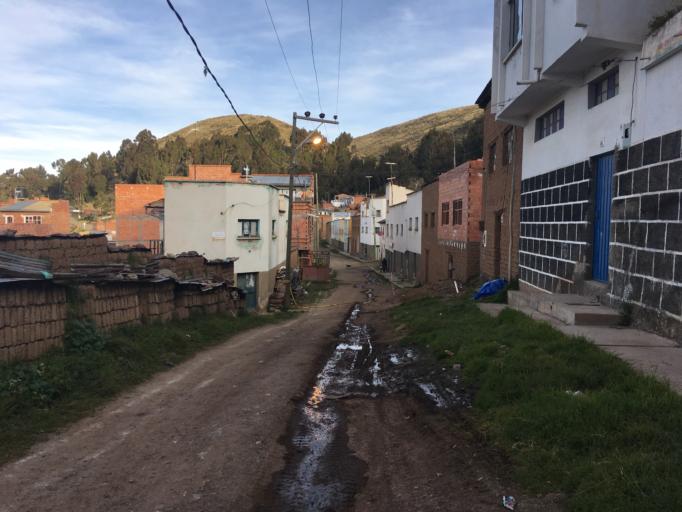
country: BO
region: La Paz
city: San Pedro
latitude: -16.2220
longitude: -68.8535
